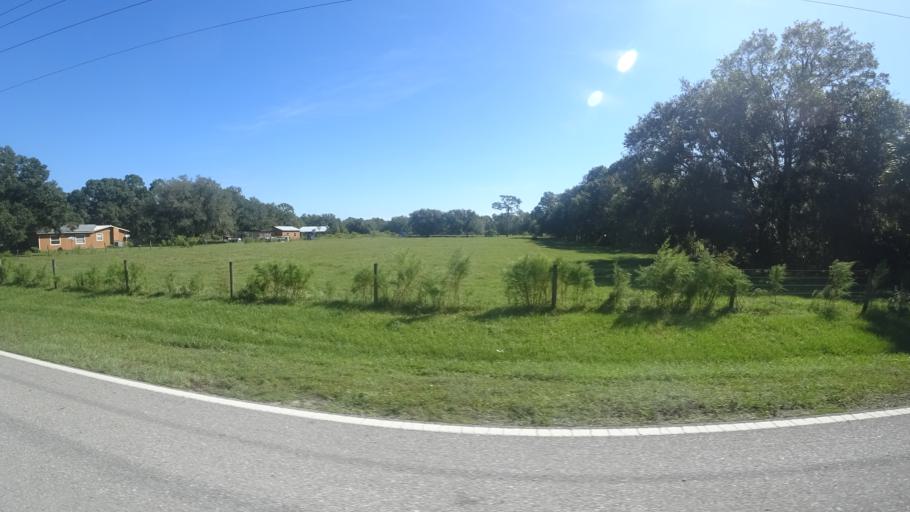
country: US
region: Florida
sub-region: Sarasota County
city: Lake Sarasota
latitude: 27.3306
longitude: -82.2695
